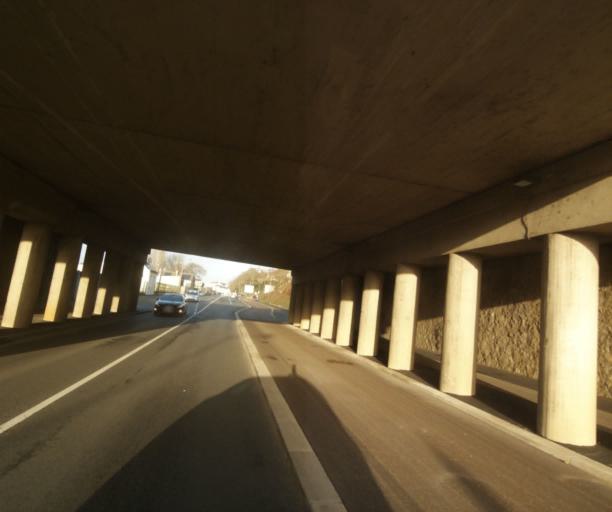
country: FR
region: Pays de la Loire
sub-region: Departement de la Sarthe
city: Le Mans
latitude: 47.9968
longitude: 0.1876
